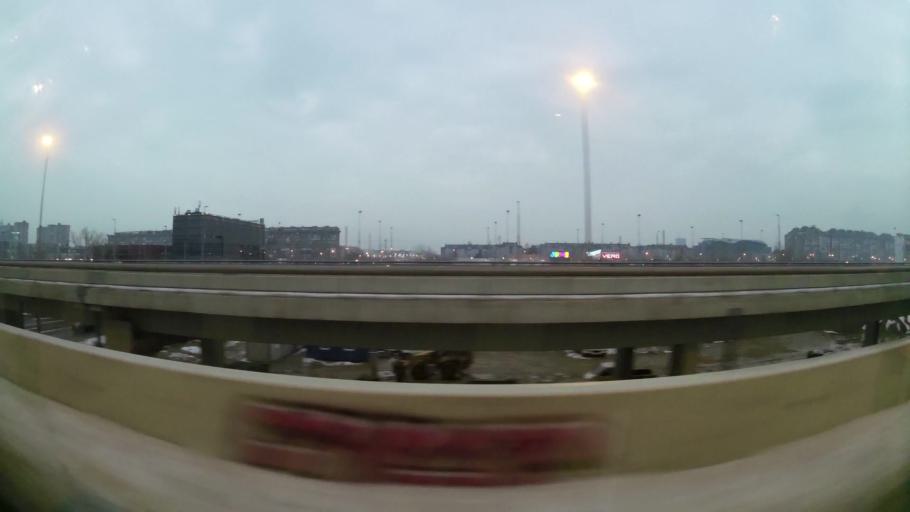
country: RS
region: Central Serbia
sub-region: Belgrade
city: Novi Beograd
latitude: 44.8077
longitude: 20.4142
